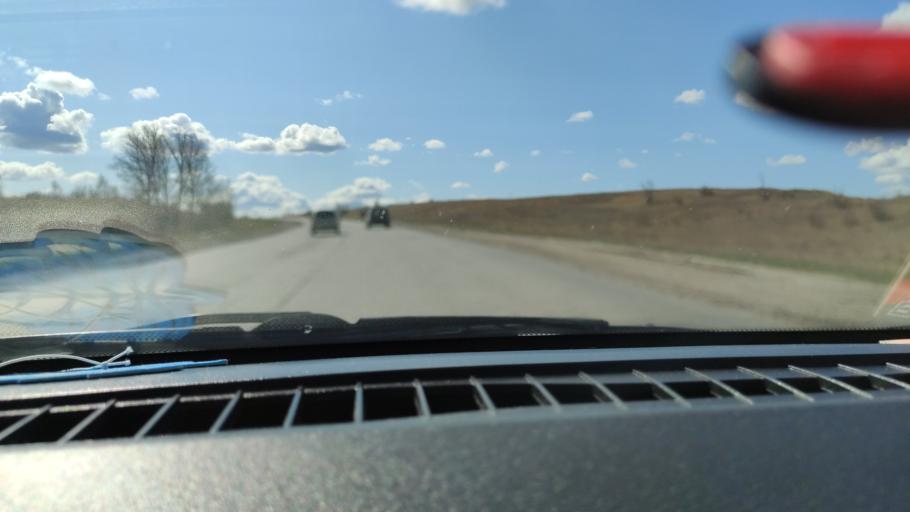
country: RU
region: Samara
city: Varlamovo
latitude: 53.1253
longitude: 48.2928
